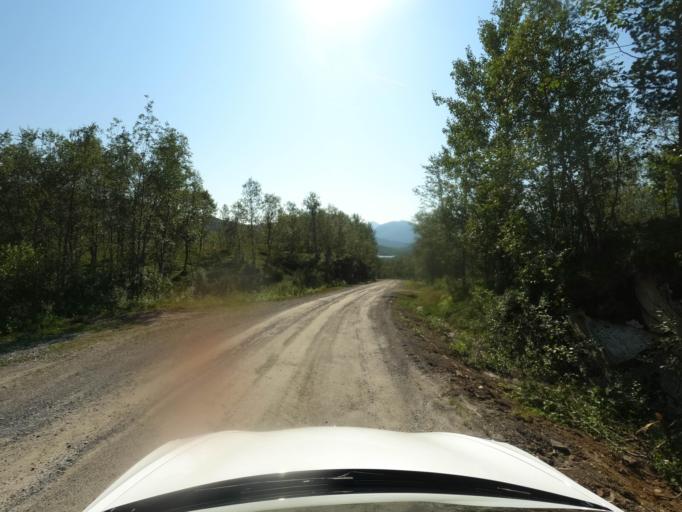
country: NO
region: Nordland
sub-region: Ballangen
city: Ballangen
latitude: 68.2614
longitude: 16.7150
